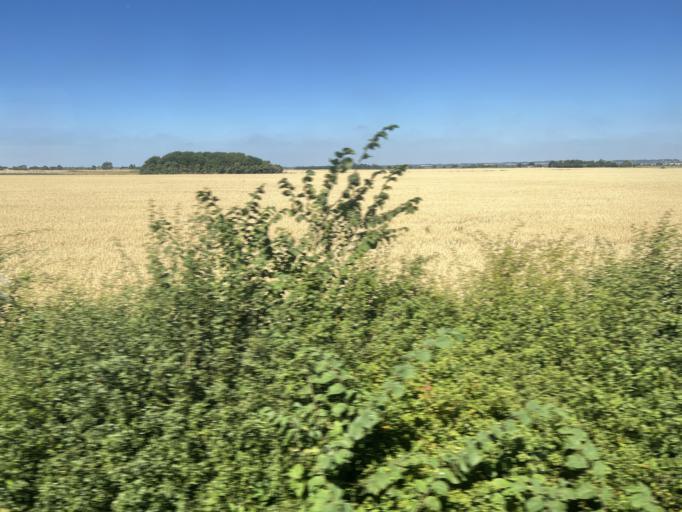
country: GB
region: England
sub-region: Lincolnshire
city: Spilsby
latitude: 53.0817
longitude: 0.0865
